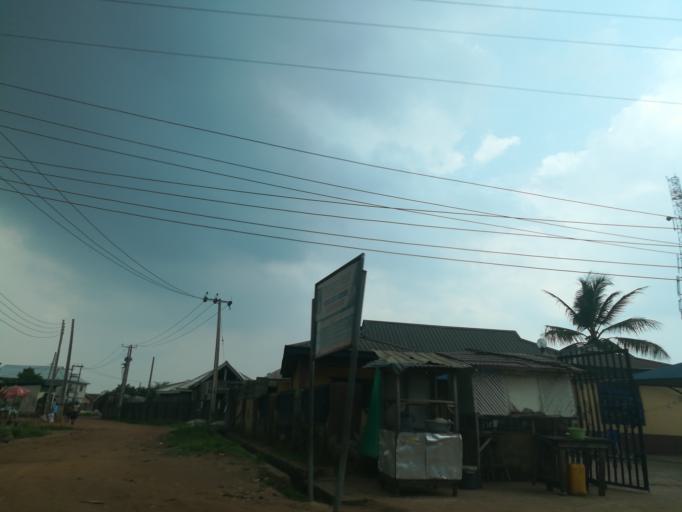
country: NG
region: Lagos
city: Ikorodu
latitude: 6.5944
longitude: 3.5888
